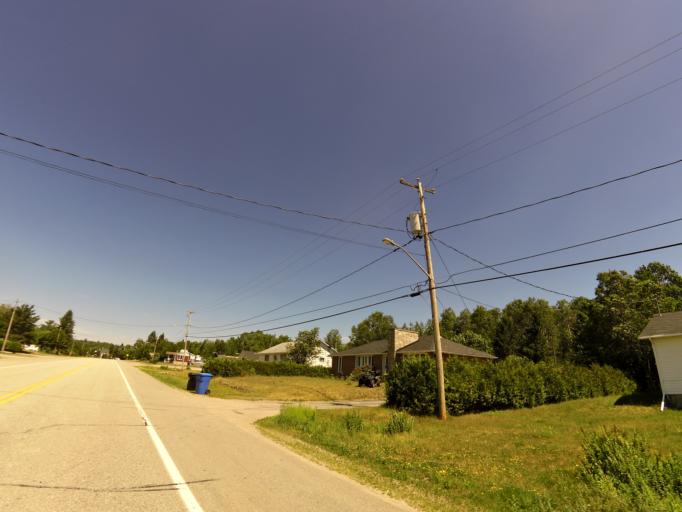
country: CA
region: Quebec
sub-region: Abitibi-Temiscamingue
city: Temiscaming
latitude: 46.7442
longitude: -79.0699
